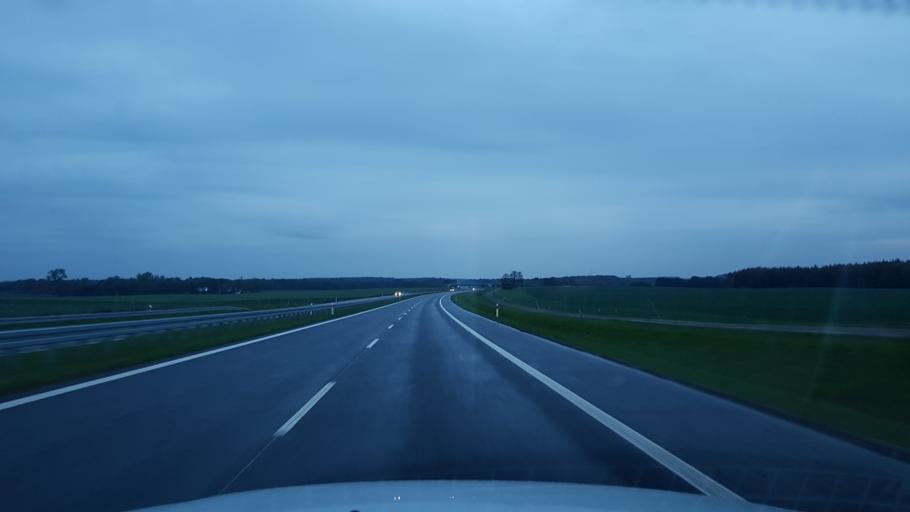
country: PL
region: West Pomeranian Voivodeship
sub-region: Powiat gryficki
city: Brojce
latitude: 53.9185
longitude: 15.3833
